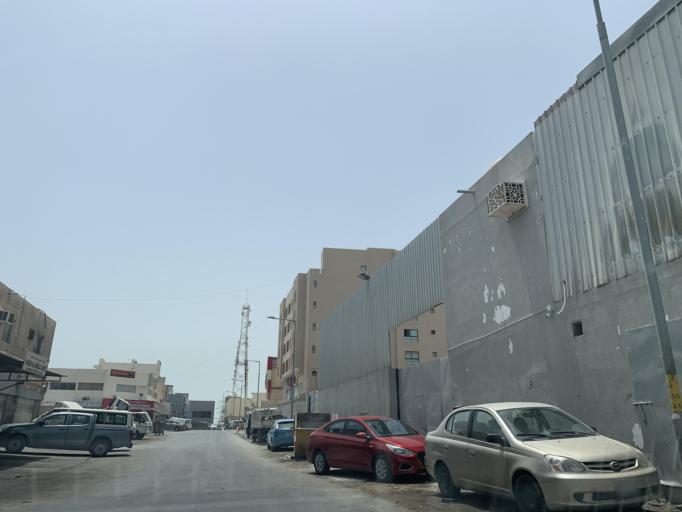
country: BH
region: Northern
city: Ar Rifa'
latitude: 26.1362
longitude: 50.5849
